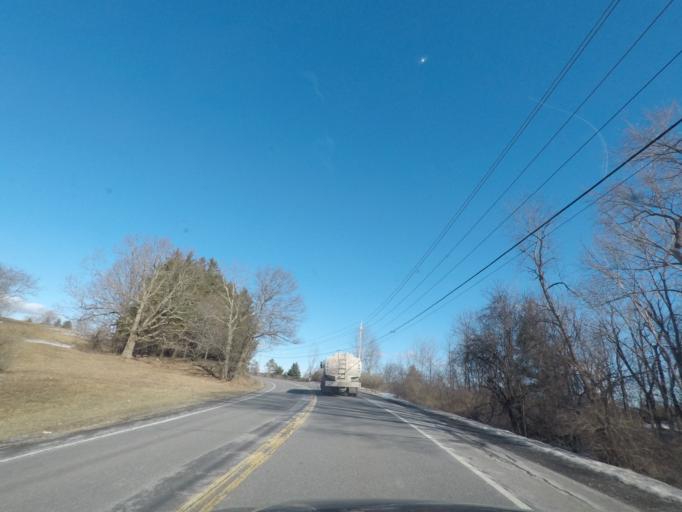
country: US
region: New York
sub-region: Columbia County
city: Chatham
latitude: 42.3512
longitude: -73.5895
